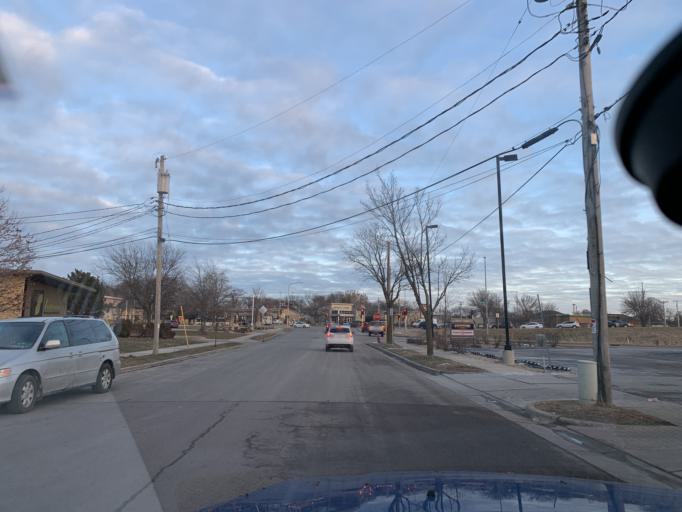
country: US
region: Wisconsin
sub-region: Dane County
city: Madison
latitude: 43.0366
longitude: -89.4070
